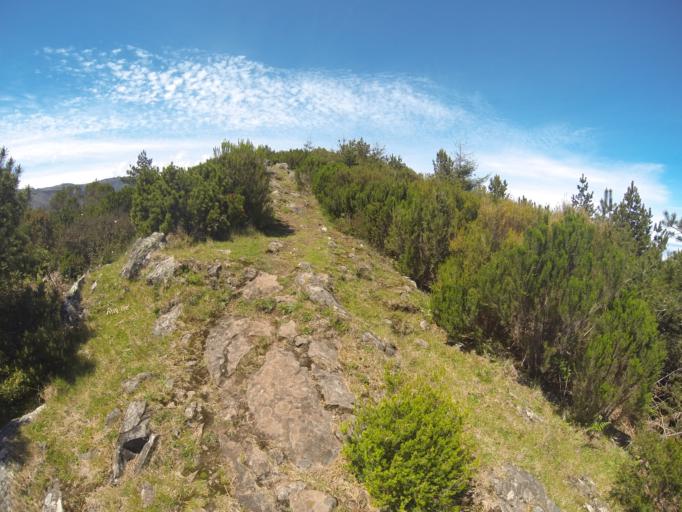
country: PT
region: Madeira
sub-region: Santa Cruz
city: Camacha
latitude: 32.7203
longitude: -16.8768
